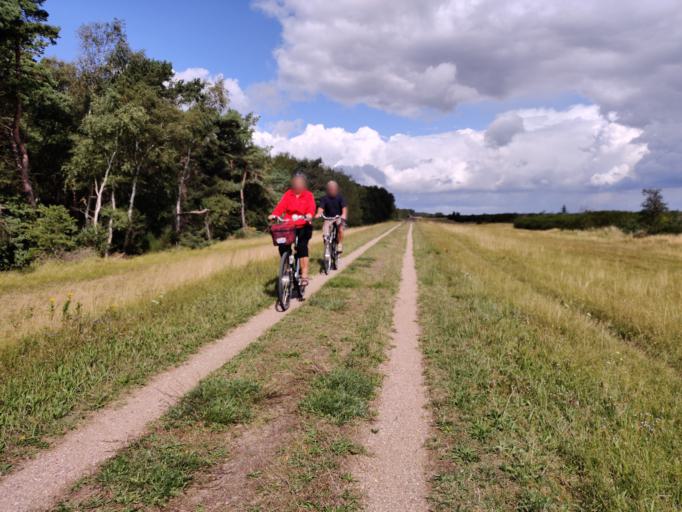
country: DK
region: Zealand
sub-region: Guldborgsund Kommune
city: Nykobing Falster
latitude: 54.6088
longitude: 11.9660
